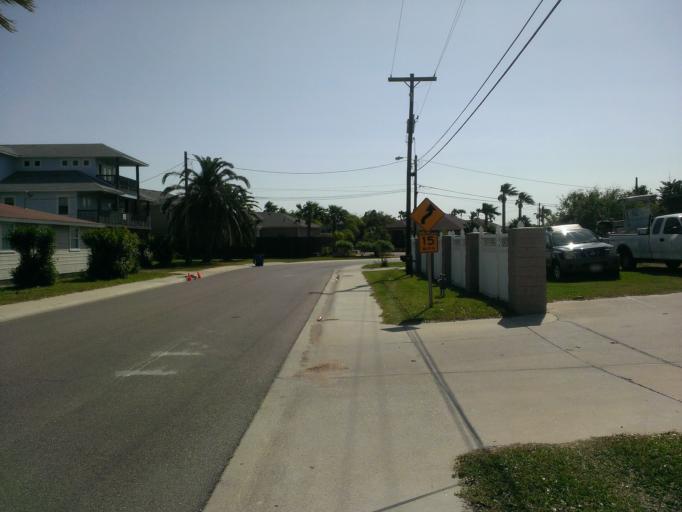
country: US
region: Texas
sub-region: Nueces County
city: Port Aransas
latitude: 27.8374
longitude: -97.0574
